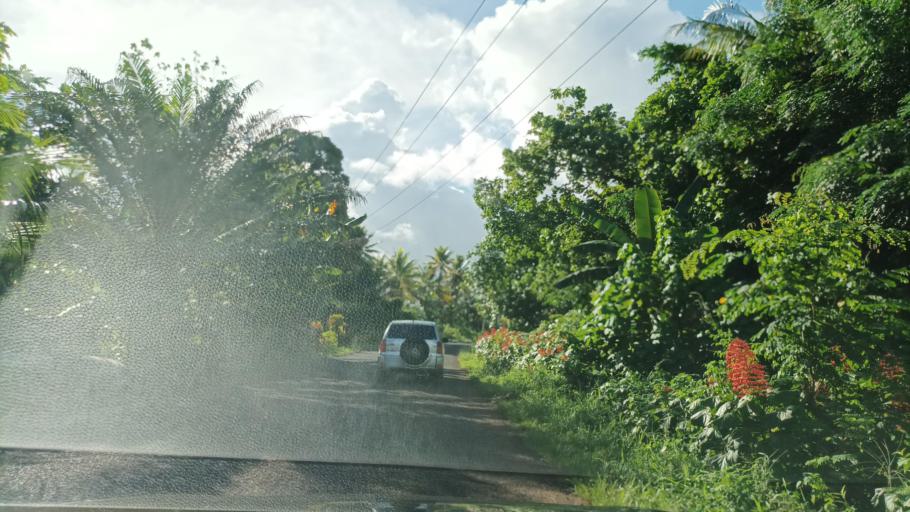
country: FM
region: Pohnpei
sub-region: Sokehs Municipality
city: Palikir - National Government Center
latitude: 6.8212
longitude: 158.1740
